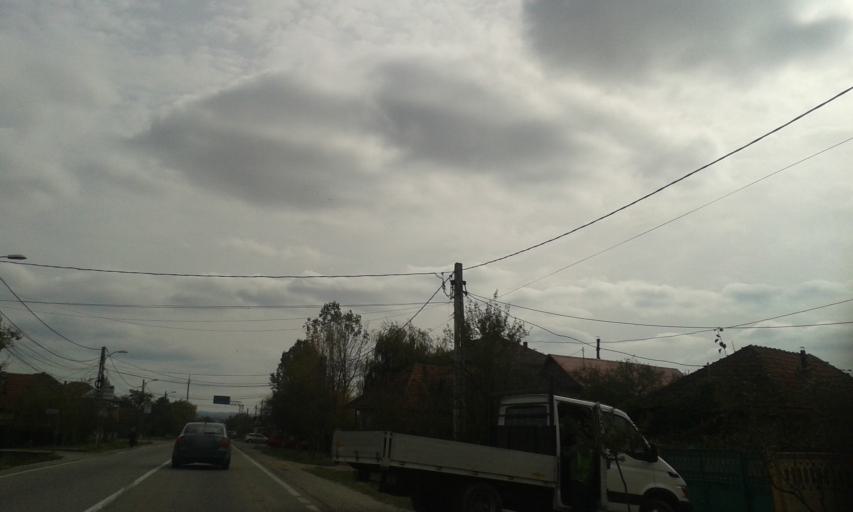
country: RO
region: Gorj
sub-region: Comuna Scoarta
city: Scoarta
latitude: 45.0188
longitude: 23.4640
